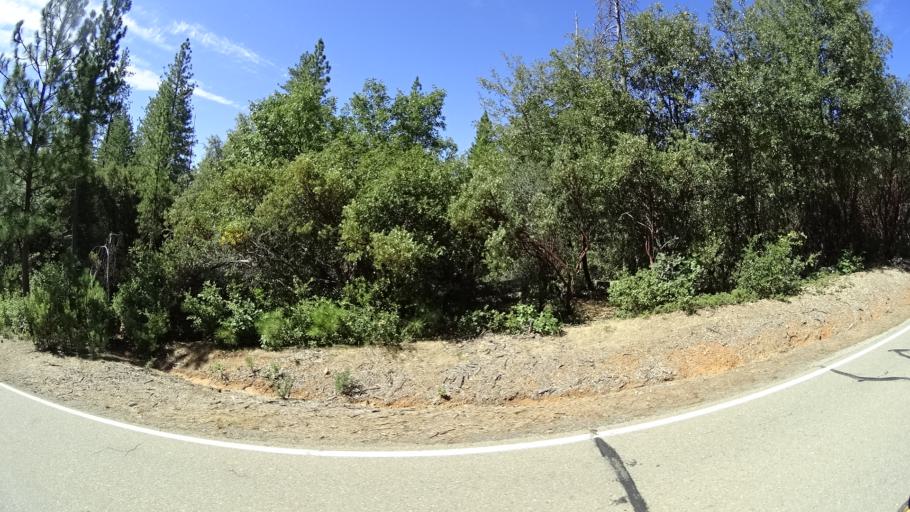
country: US
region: California
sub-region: Amador County
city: Pioneer
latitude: 38.3355
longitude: -120.5256
